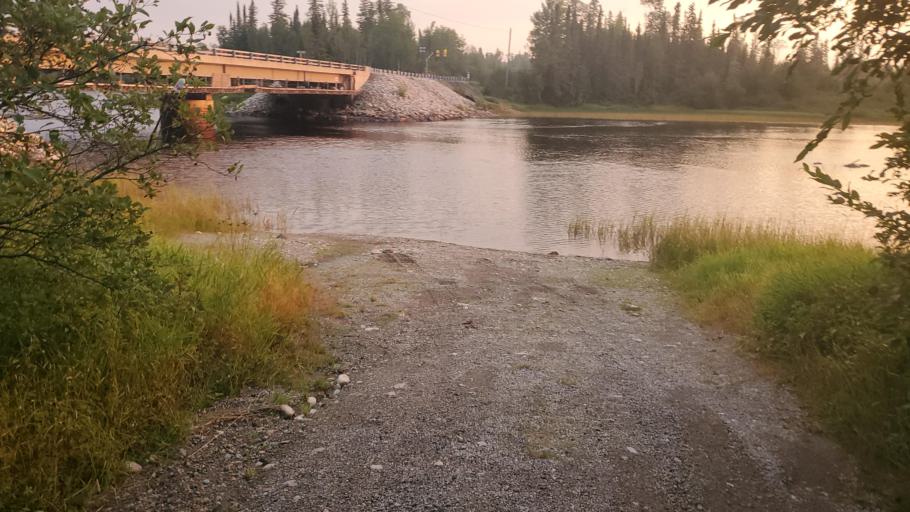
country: CA
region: Ontario
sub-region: Rainy River District
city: Atikokan
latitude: 49.6085
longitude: -91.3695
